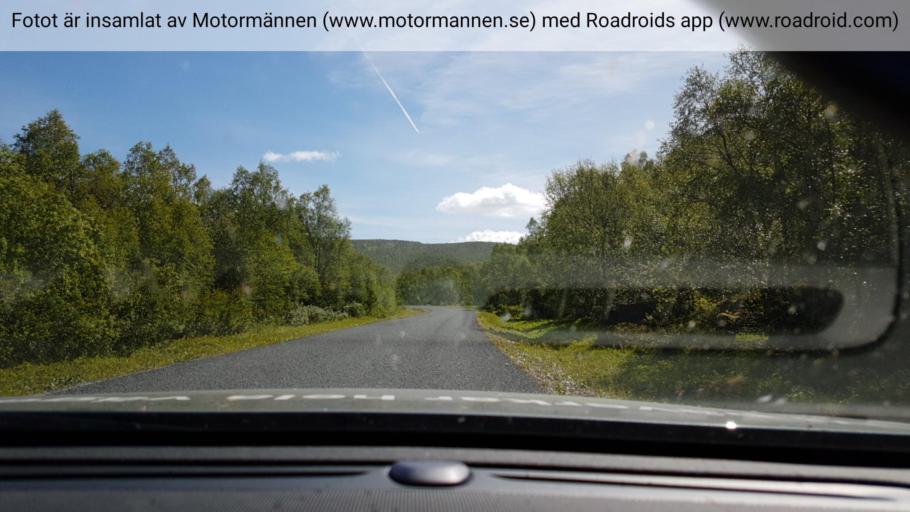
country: NO
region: Nordland
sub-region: Hattfjelldal
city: Hattfjelldal
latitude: 65.4213
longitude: 14.8498
